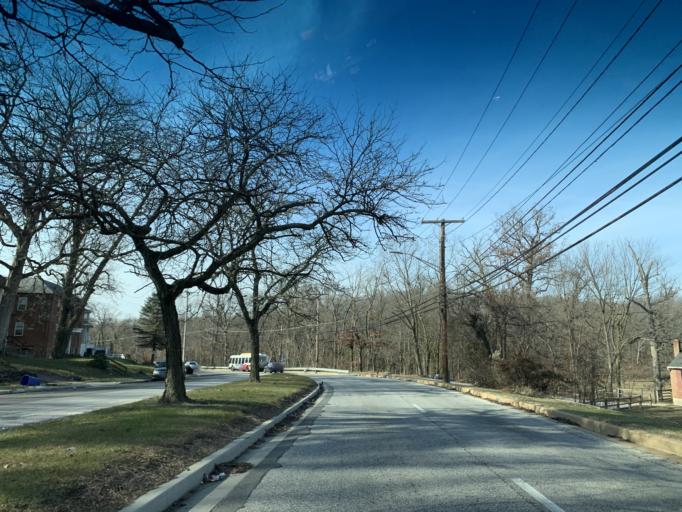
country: US
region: Maryland
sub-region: Baltimore County
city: Woodlawn
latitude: 39.3262
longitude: -76.7172
